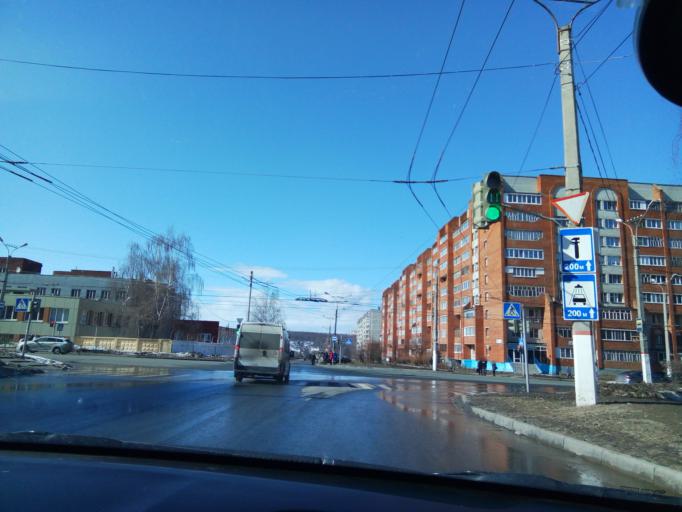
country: RU
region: Chuvashia
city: Novyye Lapsary
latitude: 56.1151
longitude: 47.1799
